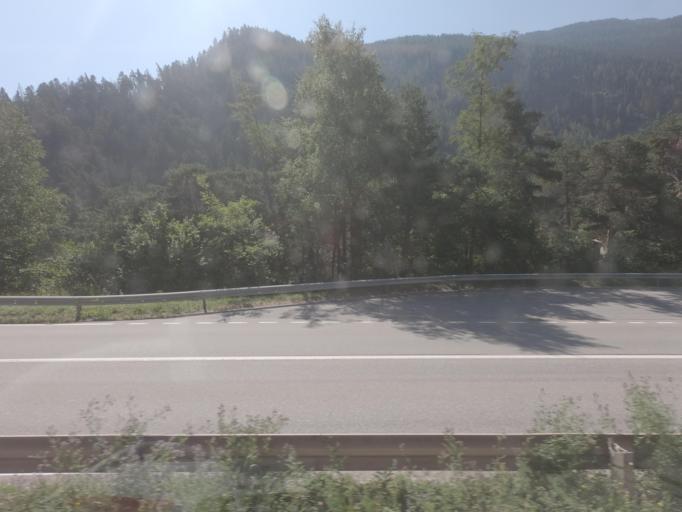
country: CH
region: Valais
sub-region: Entremont District
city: Bagnes
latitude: 46.0851
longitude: 7.1846
